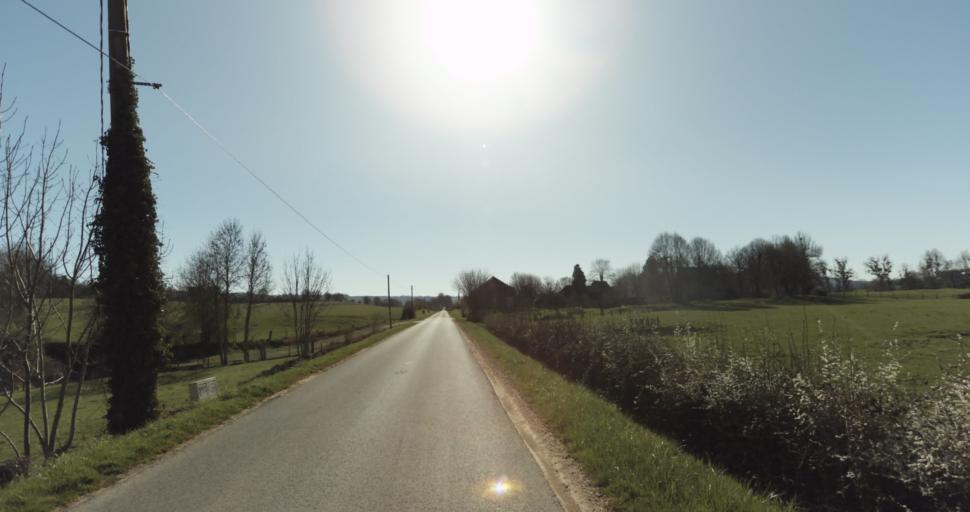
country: FR
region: Lower Normandy
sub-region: Departement du Calvados
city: Saint-Pierre-sur-Dives
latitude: 48.9741
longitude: 0.0404
